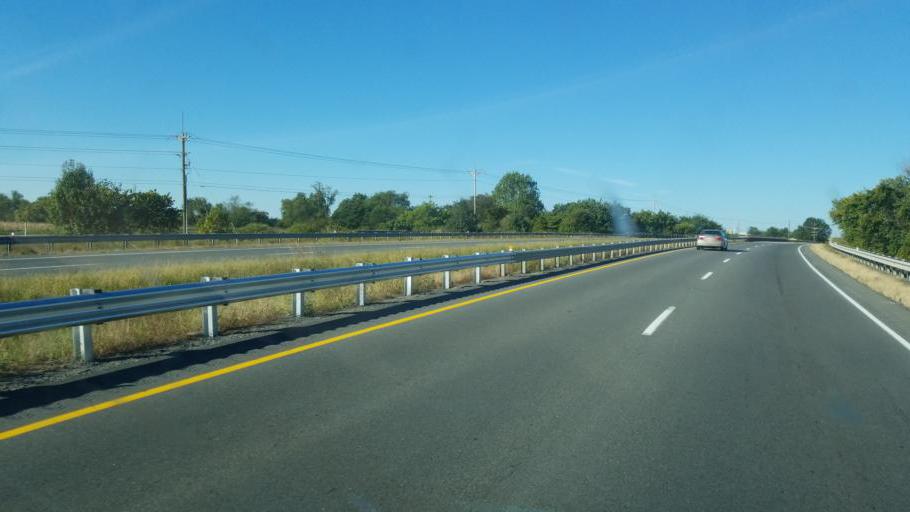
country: US
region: Virginia
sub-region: Culpeper County
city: Culpeper
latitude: 38.4455
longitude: -77.9929
